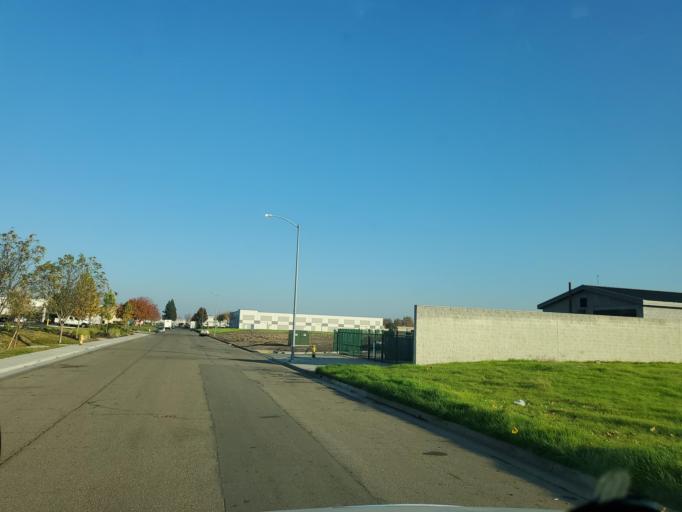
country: US
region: California
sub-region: San Joaquin County
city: Kennedy
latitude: 37.9073
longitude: -121.2196
